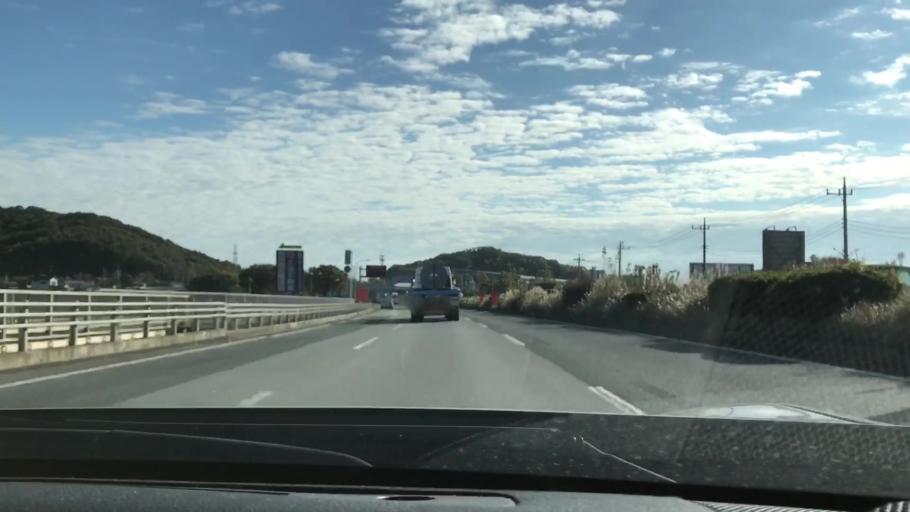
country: JP
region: Tochigi
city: Sano
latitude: 36.2956
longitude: 139.6106
